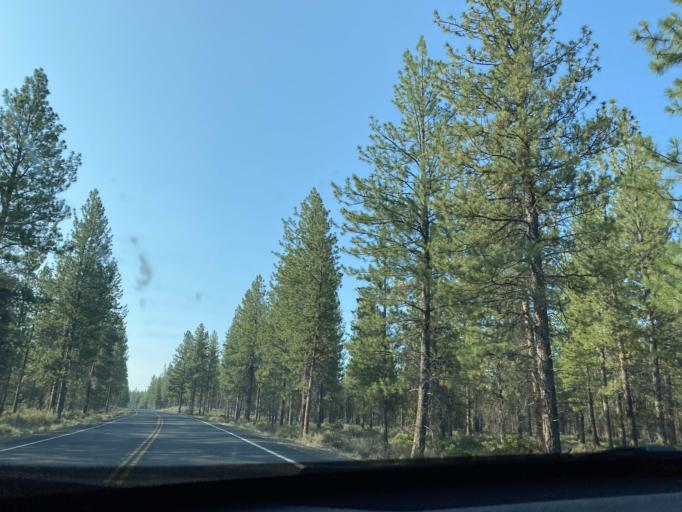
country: US
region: Oregon
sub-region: Deschutes County
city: La Pine
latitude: 43.7188
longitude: -121.4141
